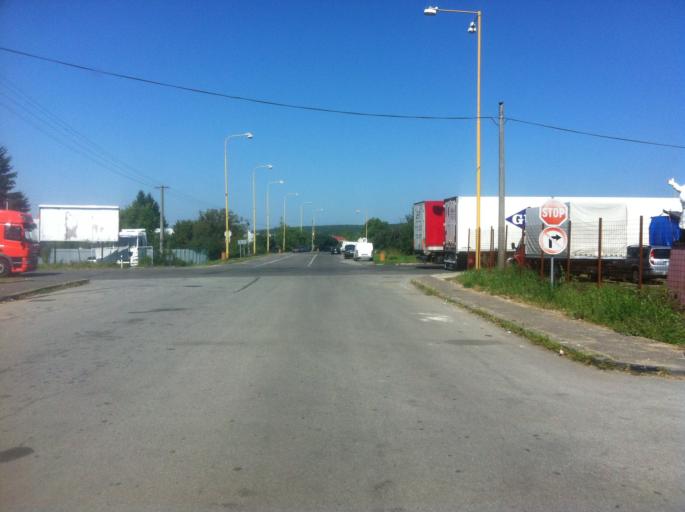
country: UA
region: Zakarpattia
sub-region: Uzhgorodskiy Raion
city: Uzhhorod
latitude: 48.6570
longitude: 22.2648
